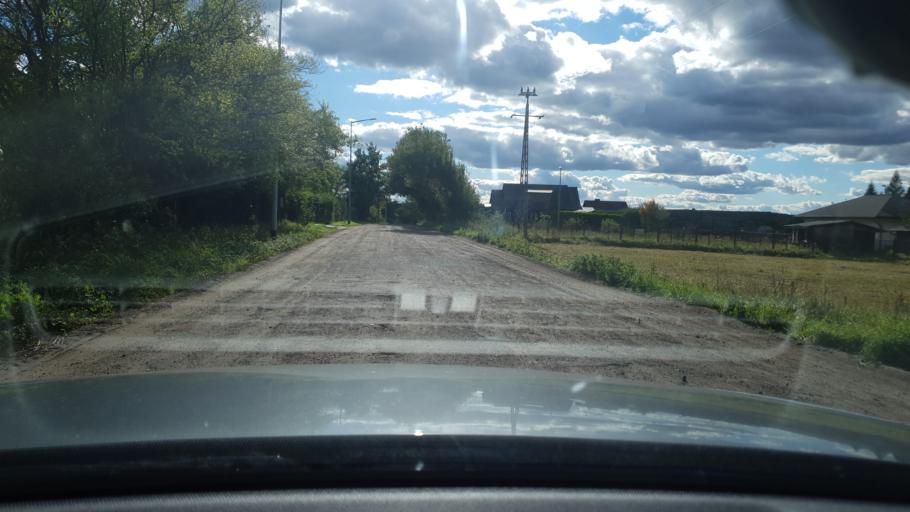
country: PL
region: Pomeranian Voivodeship
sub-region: Powiat wejherowski
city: Reda
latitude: 54.5780
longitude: 18.3113
